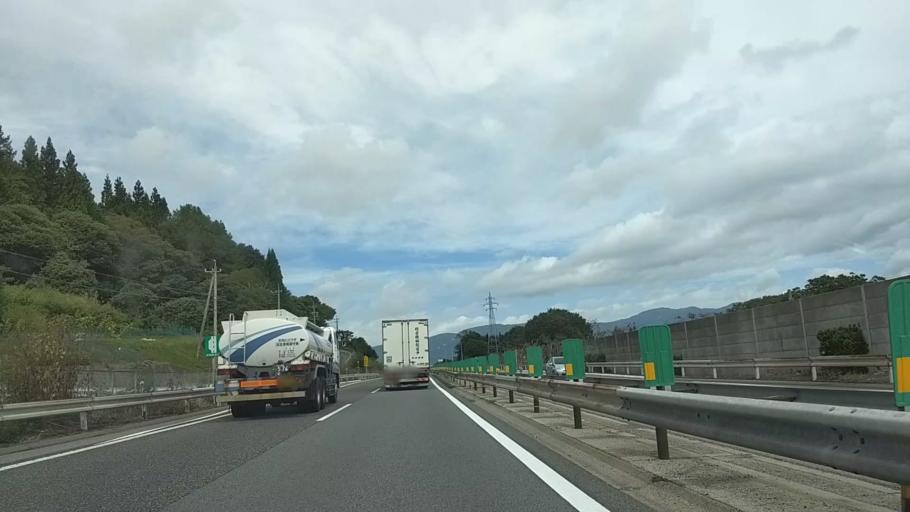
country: JP
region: Nagano
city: Suwa
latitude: 36.0206
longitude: 138.0814
